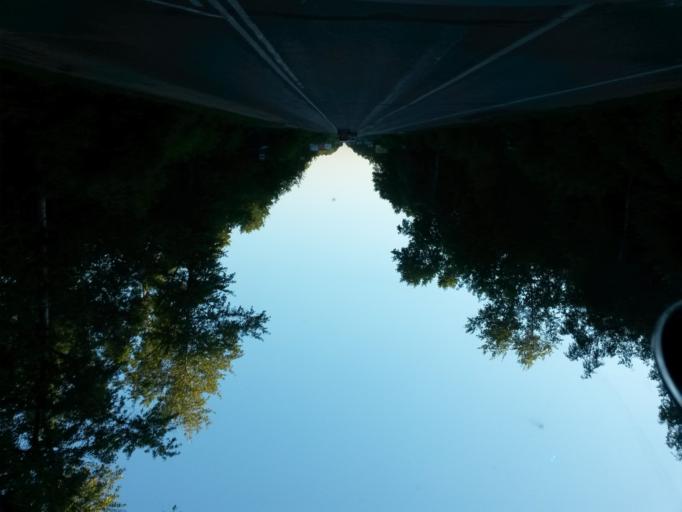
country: RU
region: Moskovskaya
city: Serpukhov
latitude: 54.9564
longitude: 37.4105
